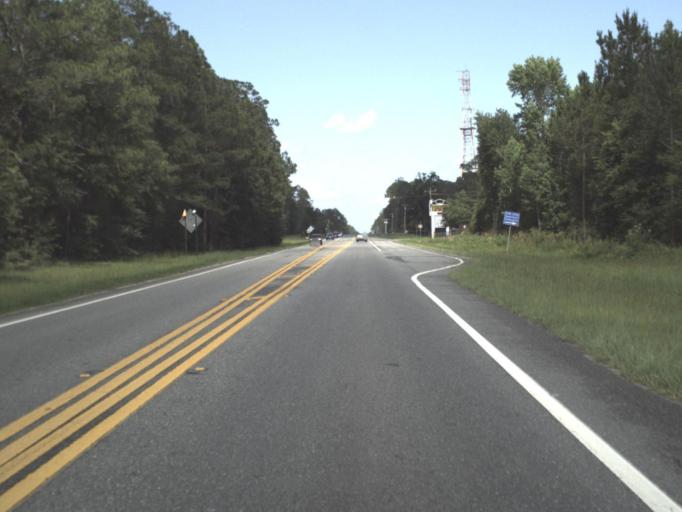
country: US
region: Florida
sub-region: Clay County
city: Green Cove Springs
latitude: 29.9834
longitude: -81.7460
